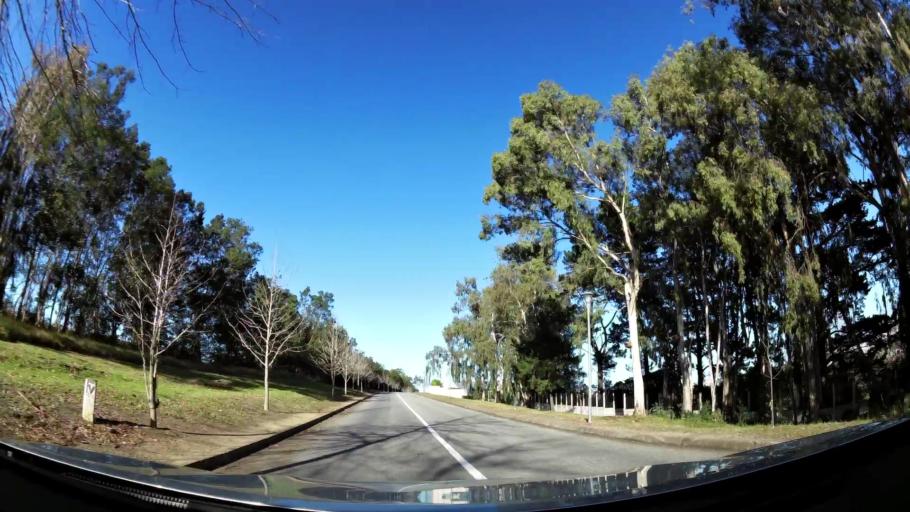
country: ZA
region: Western Cape
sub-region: Eden District Municipality
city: George
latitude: -33.9624
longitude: 22.4407
